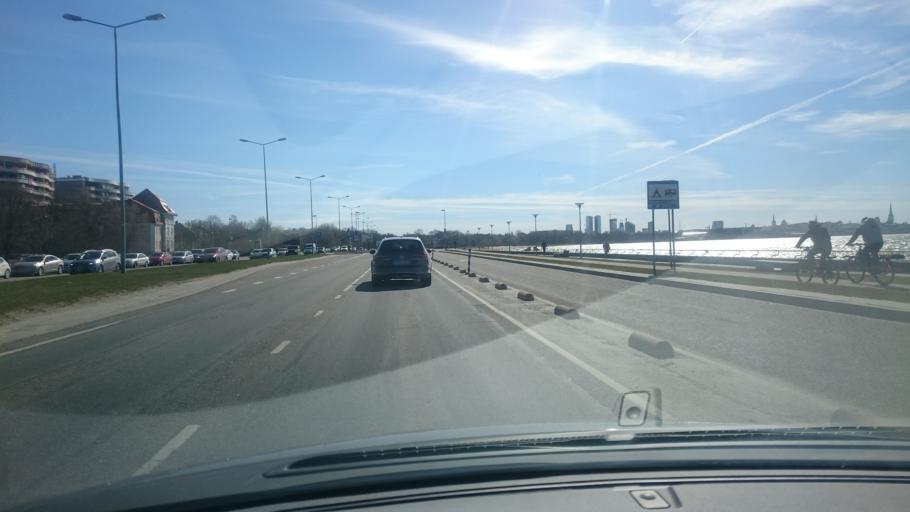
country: EE
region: Harju
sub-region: Tallinna linn
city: Tallinn
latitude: 59.4496
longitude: 24.8048
